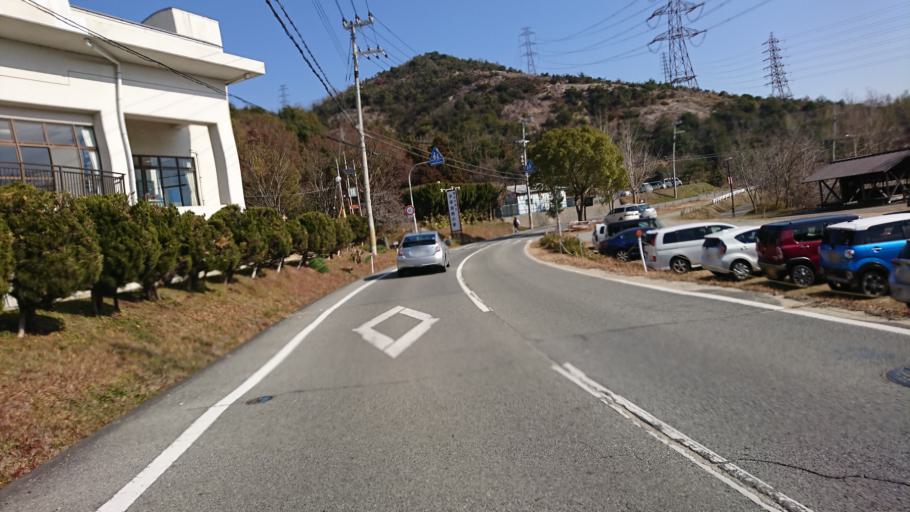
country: JP
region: Hyogo
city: Kakogawacho-honmachi
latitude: 34.7993
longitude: 134.8417
